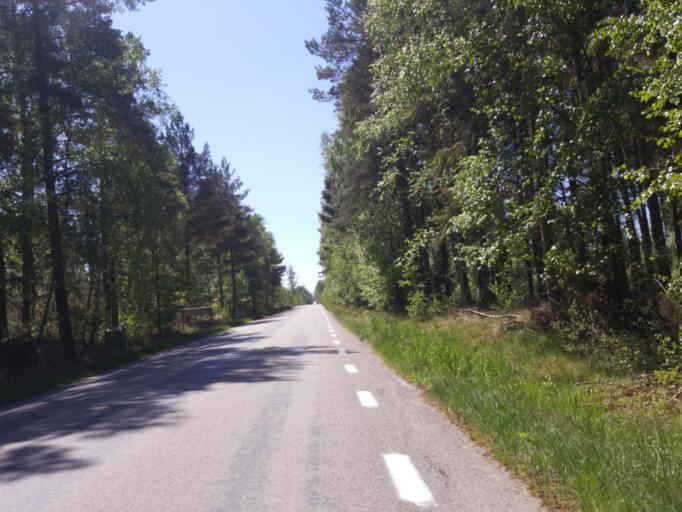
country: SE
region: Halland
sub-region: Halmstads Kommun
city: Paarp
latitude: 56.5638
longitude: 12.9744
